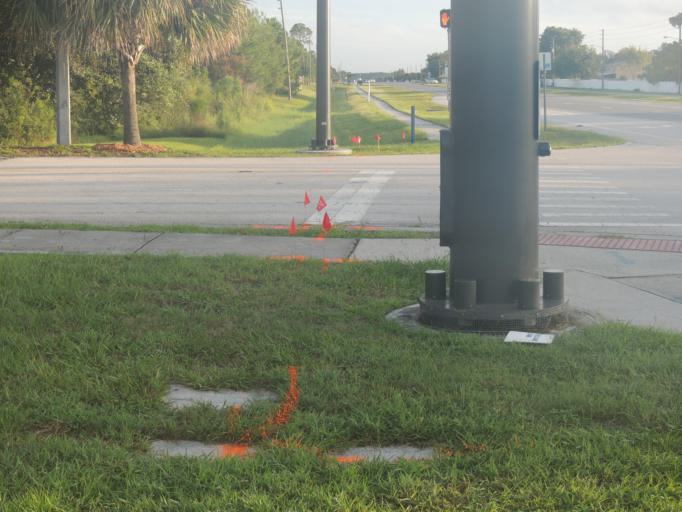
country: US
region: Florida
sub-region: Osceola County
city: Poinciana
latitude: 28.1633
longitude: -81.4402
